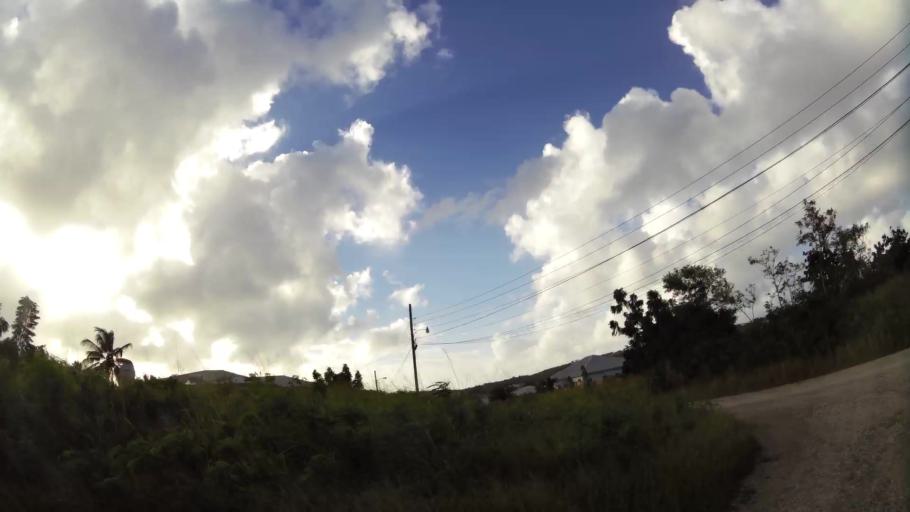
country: AG
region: Saint John
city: Saint John's
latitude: 17.1562
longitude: -61.8232
